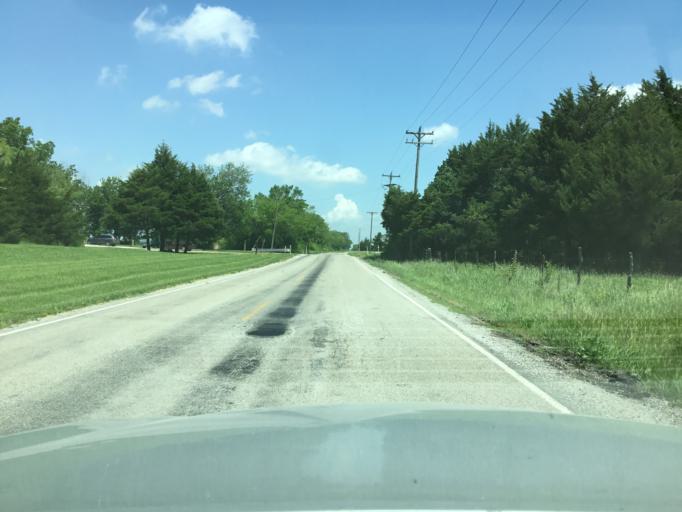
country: US
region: Kansas
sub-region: Labette County
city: Parsons
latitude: 37.3465
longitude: -95.3038
